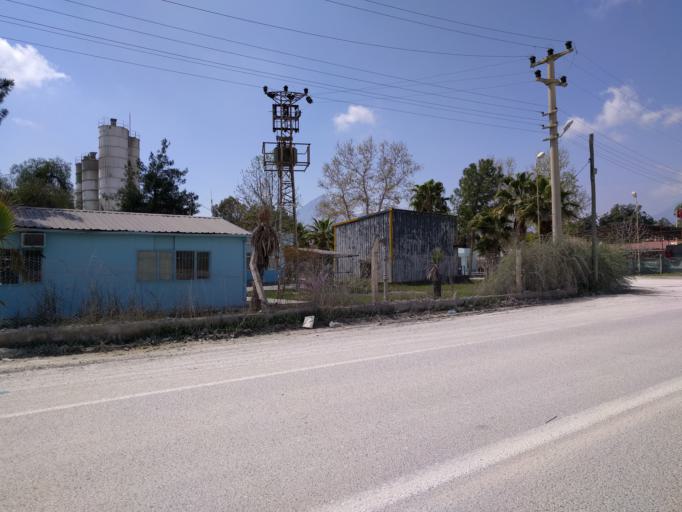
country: TR
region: Antalya
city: Cakirlar
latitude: 36.8947
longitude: 30.5982
